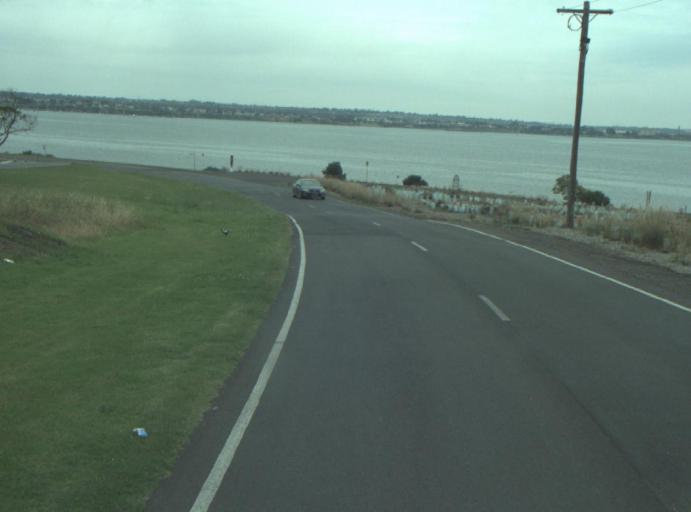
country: AU
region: Victoria
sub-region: Greater Geelong
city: East Geelong
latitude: -38.1449
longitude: 144.3841
